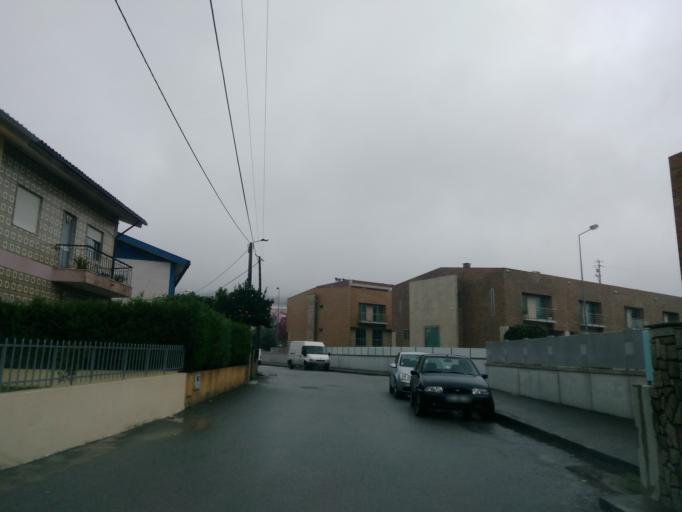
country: PT
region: Braga
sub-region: Braga
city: Adaufe
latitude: 41.5672
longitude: -8.3803
